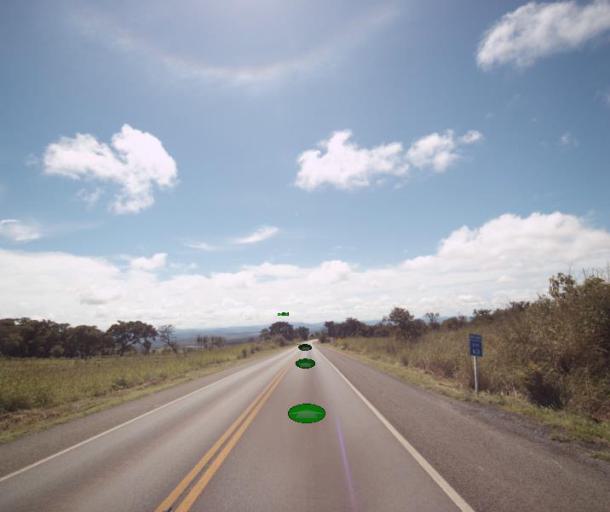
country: BR
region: Goias
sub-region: Padre Bernardo
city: Padre Bernardo
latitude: -15.1821
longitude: -48.4284
